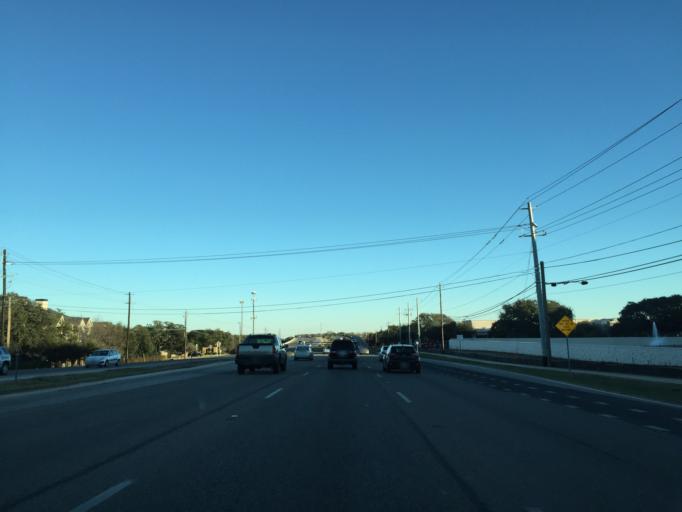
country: US
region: Texas
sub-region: Williamson County
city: Jollyville
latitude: 30.4355
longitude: -97.7336
